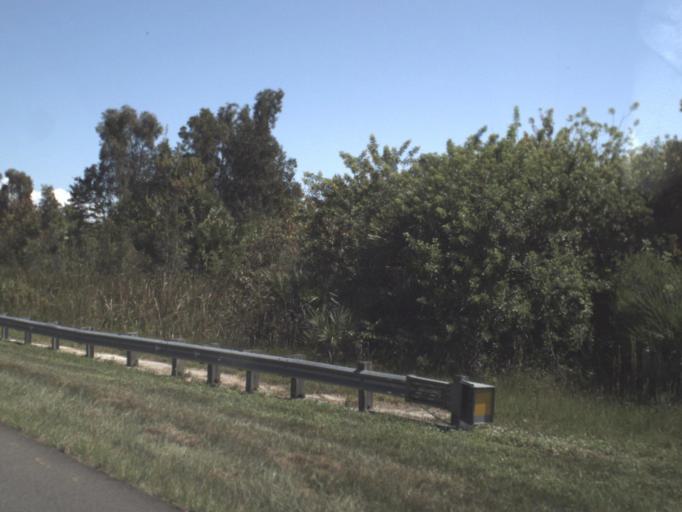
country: US
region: Florida
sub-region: Glades County
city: Buckhead Ridge
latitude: 27.0115
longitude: -81.0319
